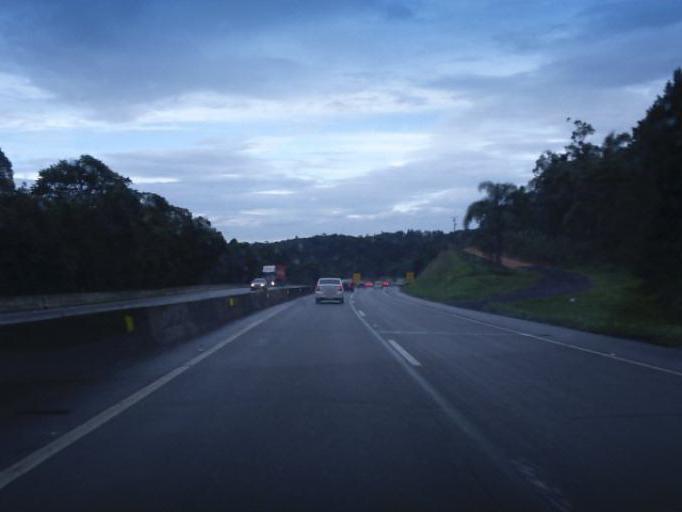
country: BR
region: Parana
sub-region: Sao Jose Dos Pinhais
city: Sao Jose dos Pinhais
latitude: -25.8446
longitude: -49.0608
